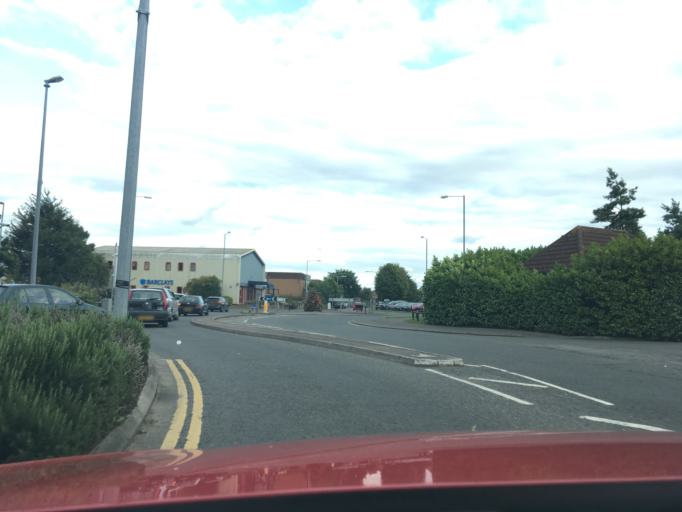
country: GB
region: England
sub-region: Gloucestershire
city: Swindon
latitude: 51.9174
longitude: -2.1037
